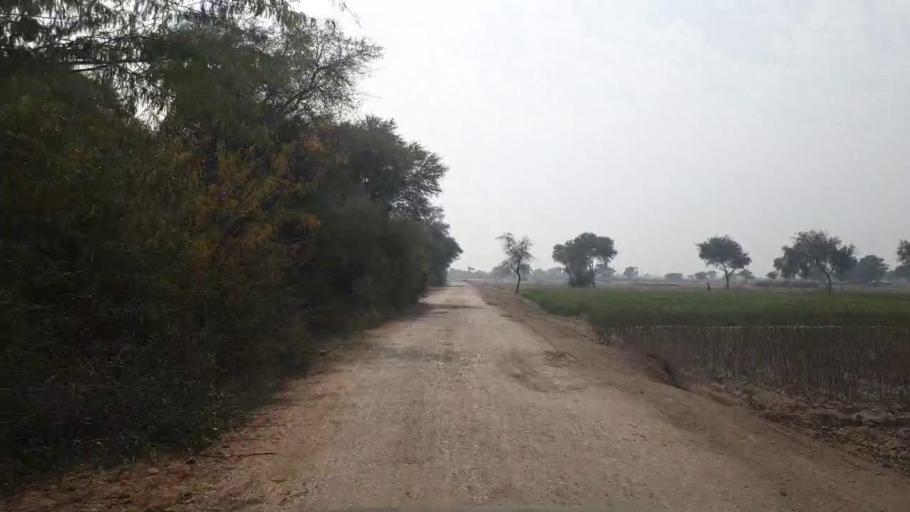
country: PK
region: Sindh
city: Hala
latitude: 25.7793
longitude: 68.4364
